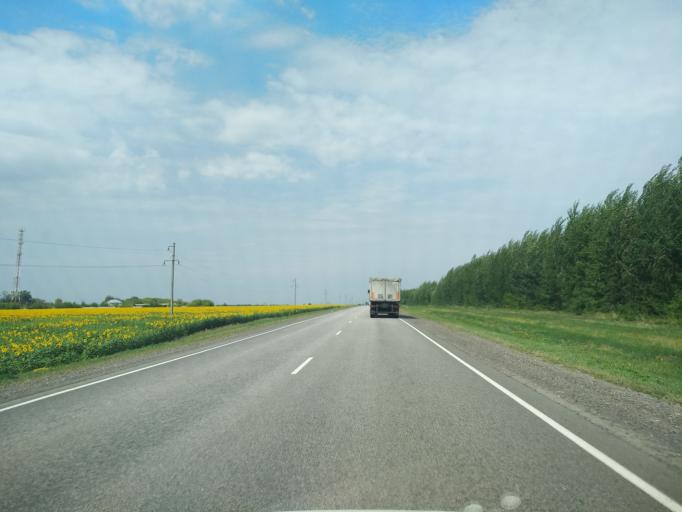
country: RU
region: Voronezj
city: Orlovo
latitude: 51.6765
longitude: 39.7030
